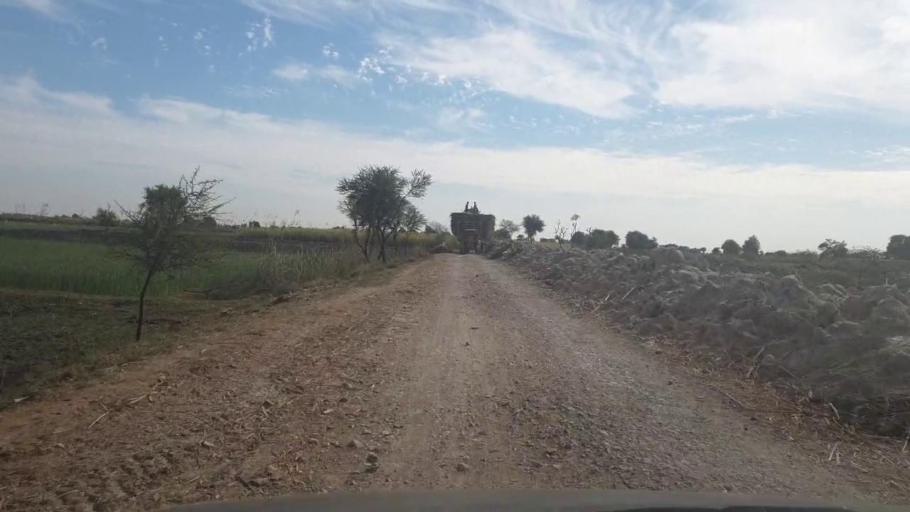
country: PK
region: Sindh
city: Mirwah Gorchani
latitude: 25.4206
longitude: 69.2011
